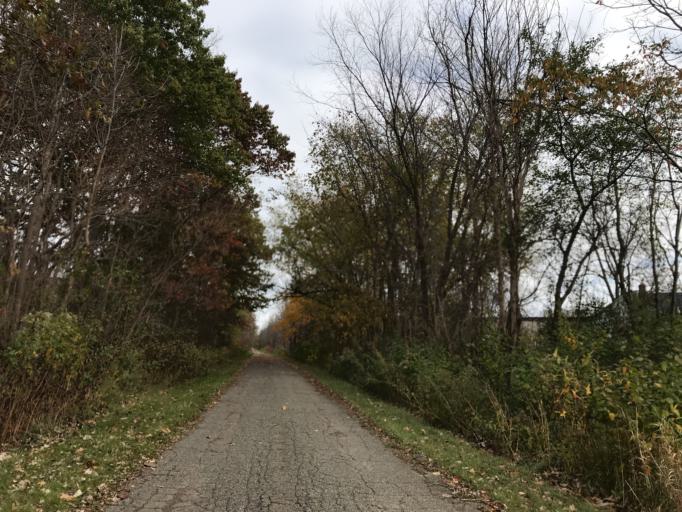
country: US
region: Michigan
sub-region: Oakland County
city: South Lyon
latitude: 42.4997
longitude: -83.6205
